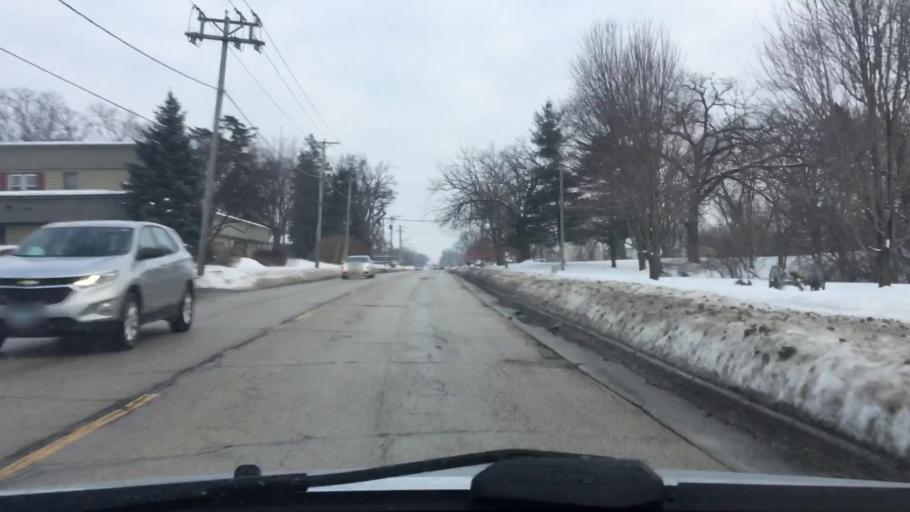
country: US
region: Illinois
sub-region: McHenry County
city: Woodstock
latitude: 42.3072
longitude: -88.4372
